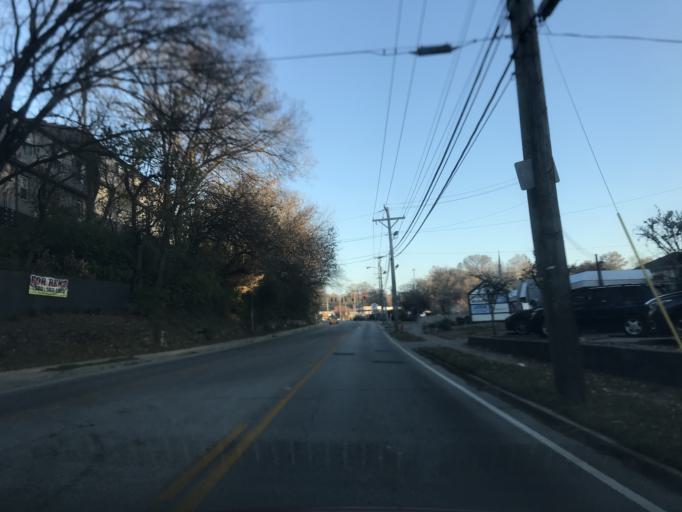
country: US
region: Indiana
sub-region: Clark County
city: Jeffersonville
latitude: 38.2593
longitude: -85.7061
